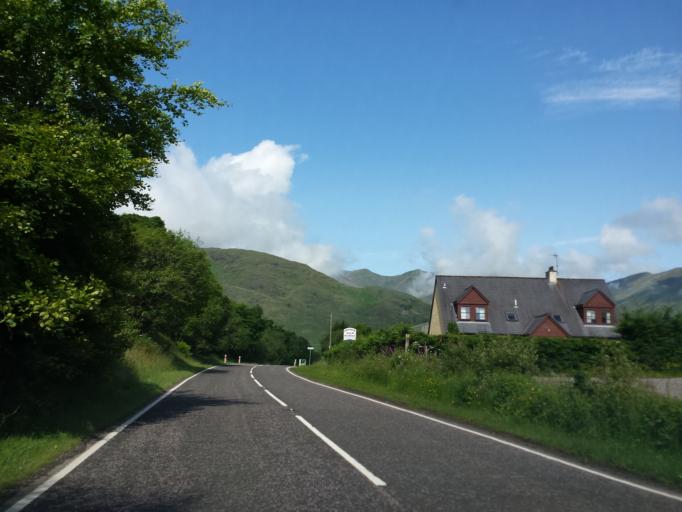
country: GB
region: Scotland
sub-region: Argyll and Bute
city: Garelochhead
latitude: 56.4043
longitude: -5.0084
